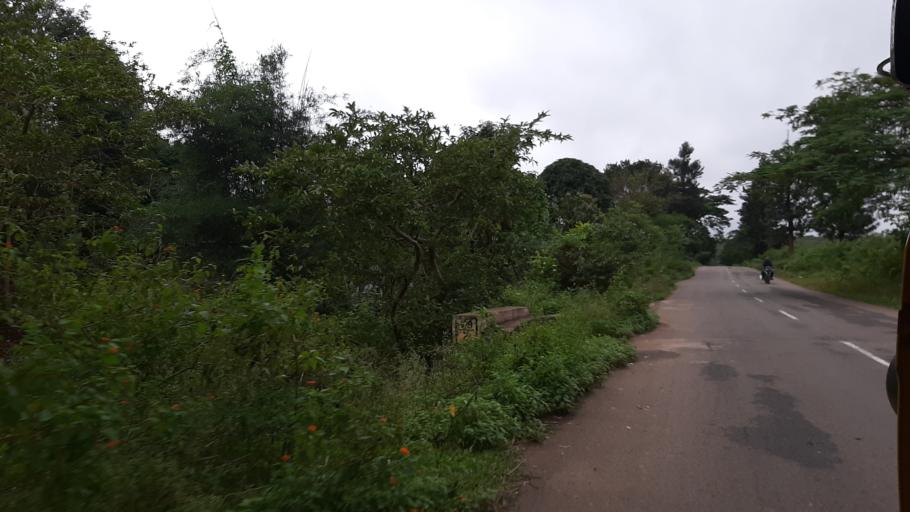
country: IN
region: Andhra Pradesh
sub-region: Vizianagaram District
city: Salur
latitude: 18.3003
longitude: 82.9113
